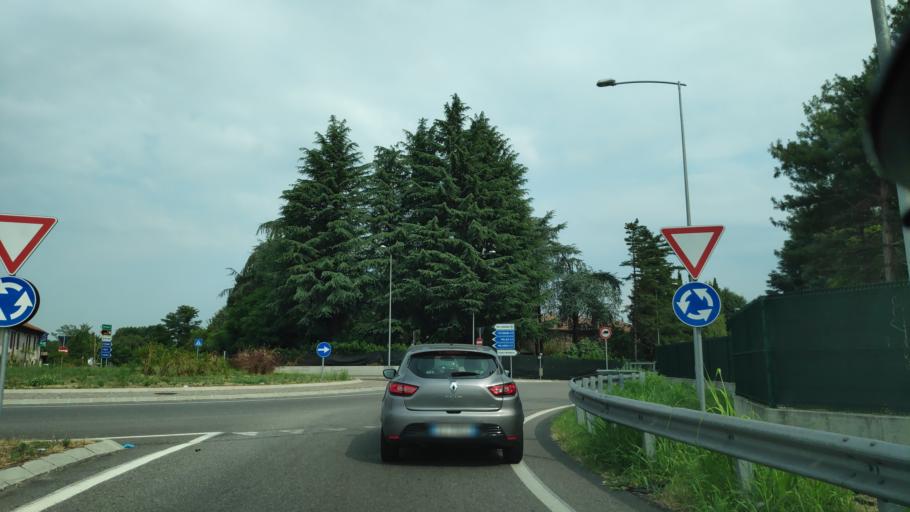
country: IT
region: Lombardy
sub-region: Citta metropolitana di Milano
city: Vizzolo Predabissi
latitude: 45.3520
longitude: 9.3407
